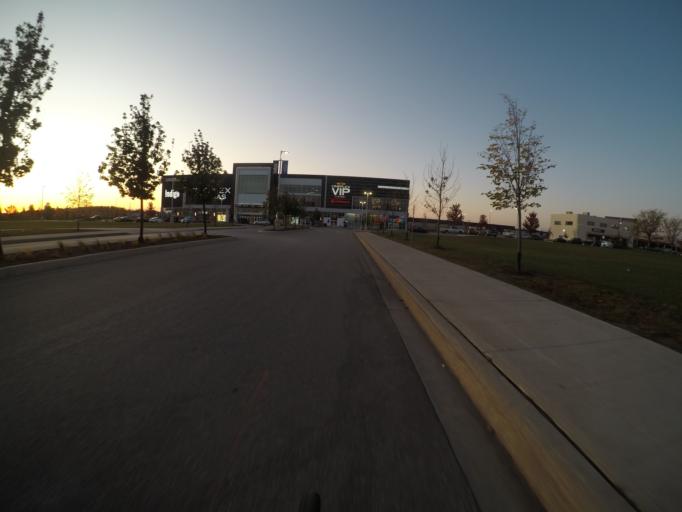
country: CA
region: Ontario
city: Kitchener
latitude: 43.4212
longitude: -80.4393
